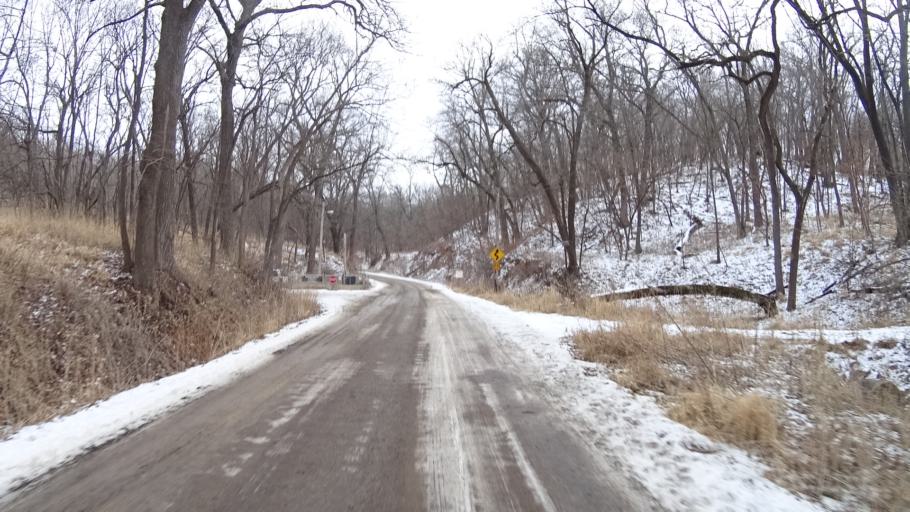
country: US
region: Nebraska
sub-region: Sarpy County
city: Bellevue
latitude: 41.1713
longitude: -95.9063
